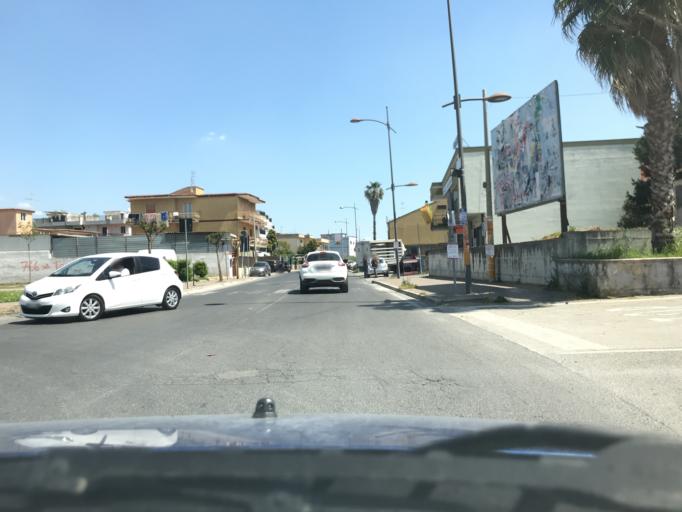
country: IT
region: Campania
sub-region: Provincia di Napoli
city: Villaricca
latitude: 40.9183
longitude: 14.1820
